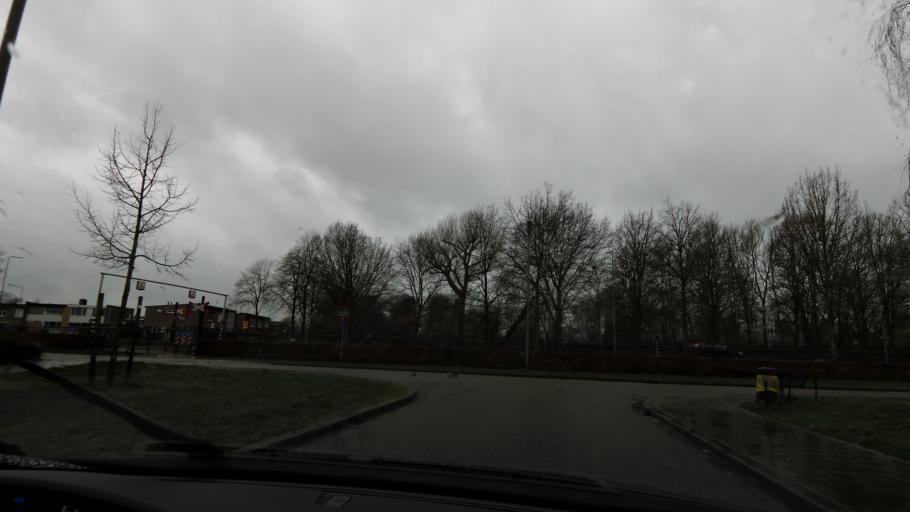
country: NL
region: Limburg
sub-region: Gemeente Sittard-Geleen
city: Born
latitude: 51.0310
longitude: 5.8143
